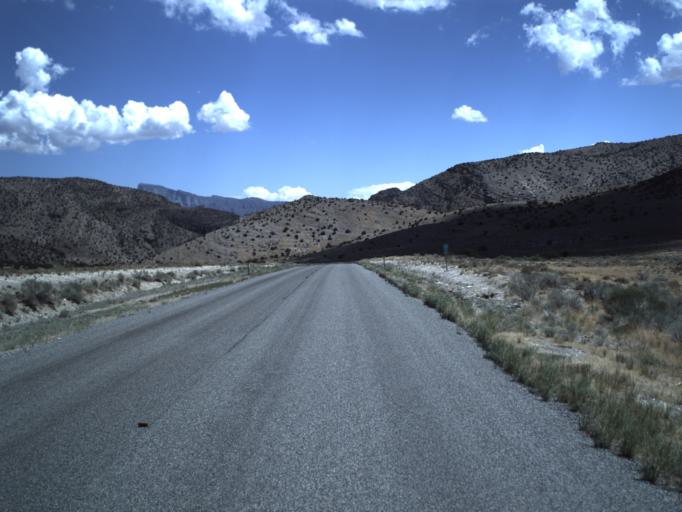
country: US
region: Utah
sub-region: Beaver County
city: Milford
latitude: 39.0778
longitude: -113.6176
